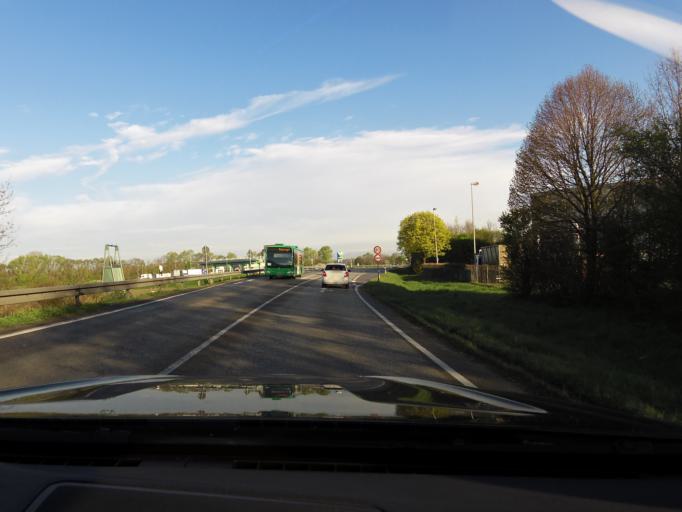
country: DE
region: Bavaria
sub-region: Upper Bavaria
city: Oberding
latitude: 48.3586
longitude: 11.8268
